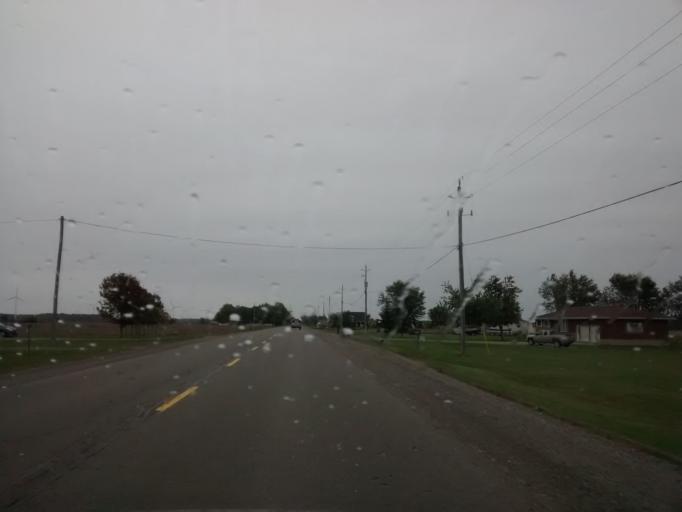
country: CA
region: Ontario
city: Ancaster
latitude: 42.8450
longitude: -79.8639
